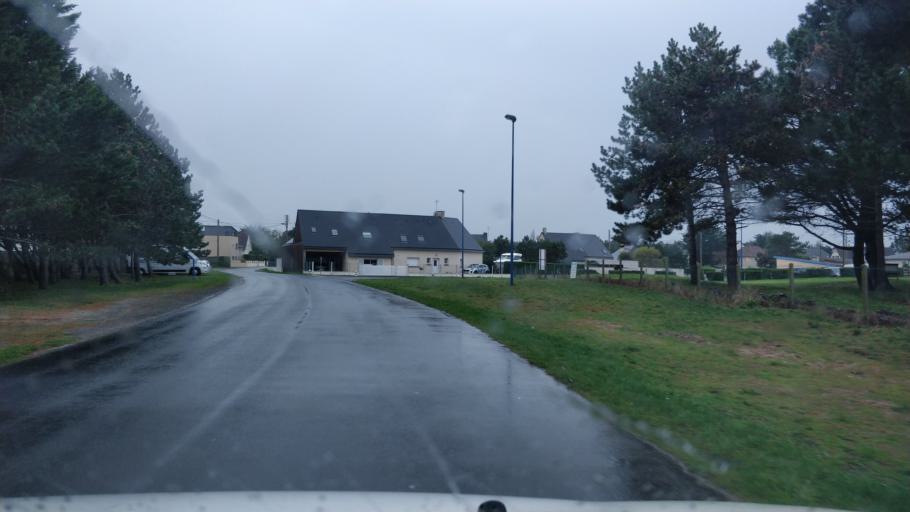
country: FR
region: Lower Normandy
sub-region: Departement de la Manche
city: Brehal
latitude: 48.9044
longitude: -1.5644
